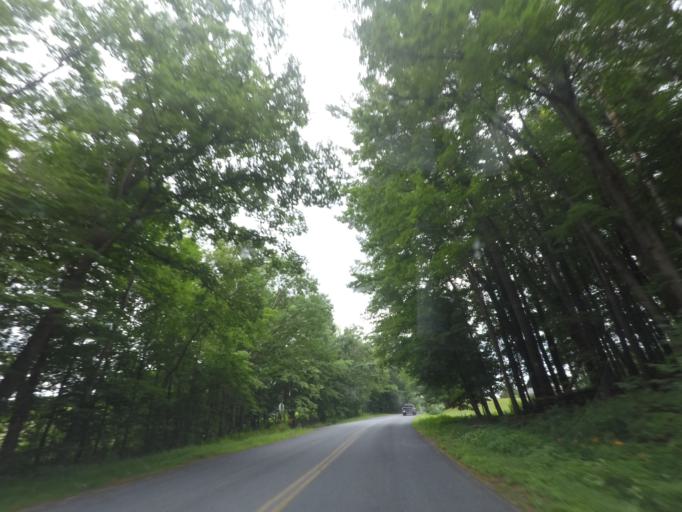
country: US
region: New York
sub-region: Saratoga County
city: Stillwater
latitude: 42.8506
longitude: -73.5428
